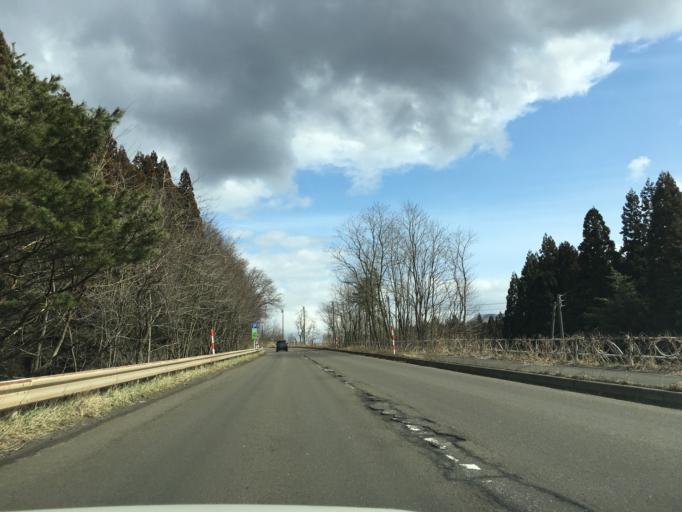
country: JP
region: Akita
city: Odate
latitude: 40.2168
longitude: 140.6313
